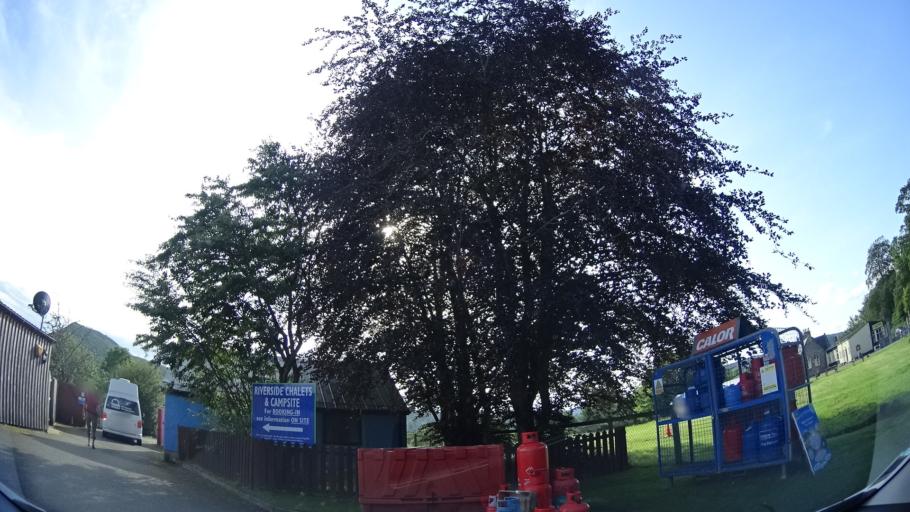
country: GB
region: Scotland
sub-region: Highland
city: Muir of Ord
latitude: 57.5694
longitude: -4.5810
